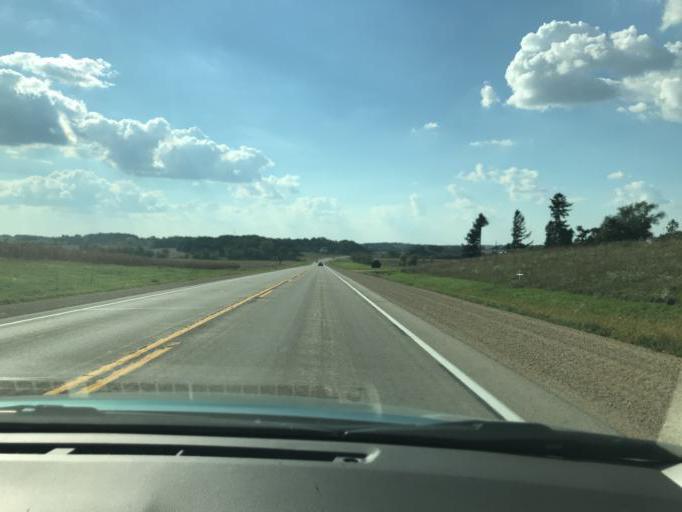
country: US
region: Wisconsin
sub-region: Green County
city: Brodhead
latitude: 42.5885
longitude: -89.4752
